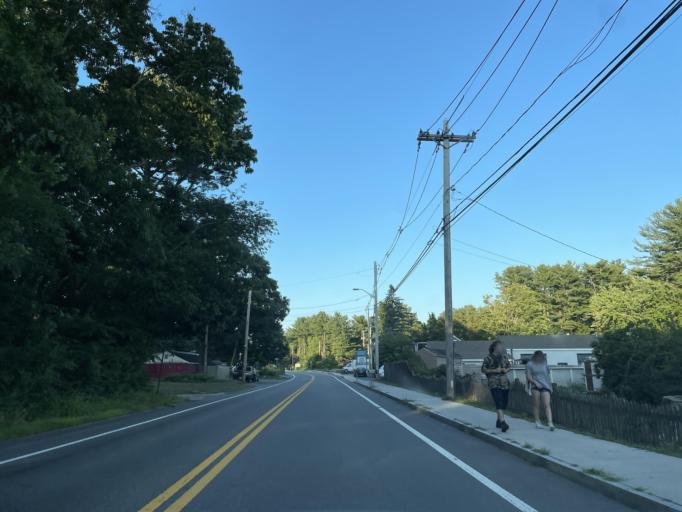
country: US
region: Massachusetts
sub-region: Plymouth County
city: North Pembroke
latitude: 42.0615
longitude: -70.8251
